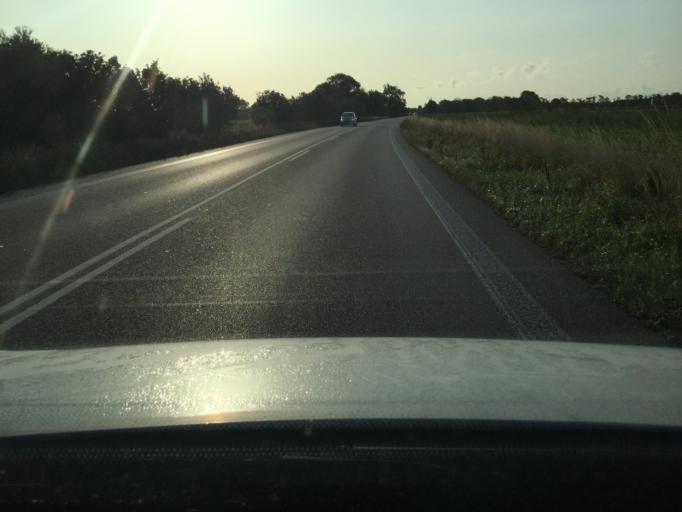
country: DK
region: Zealand
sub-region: Lolland Kommune
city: Nakskov
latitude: 54.8039
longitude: 11.2415
